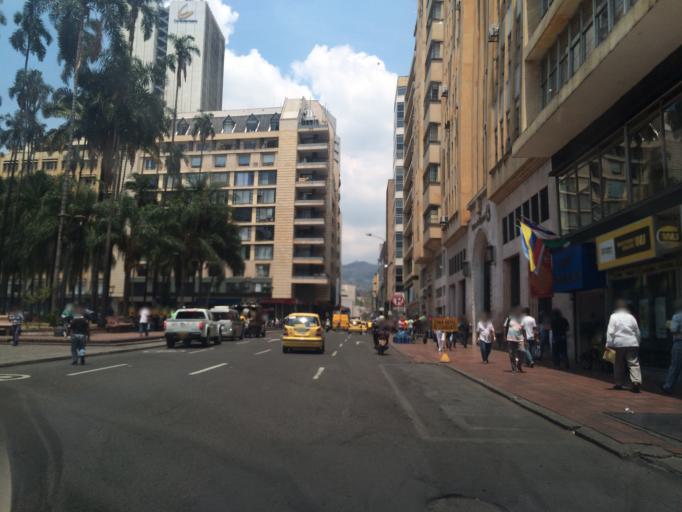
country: CO
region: Valle del Cauca
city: Cali
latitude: 3.4525
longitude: -76.5322
